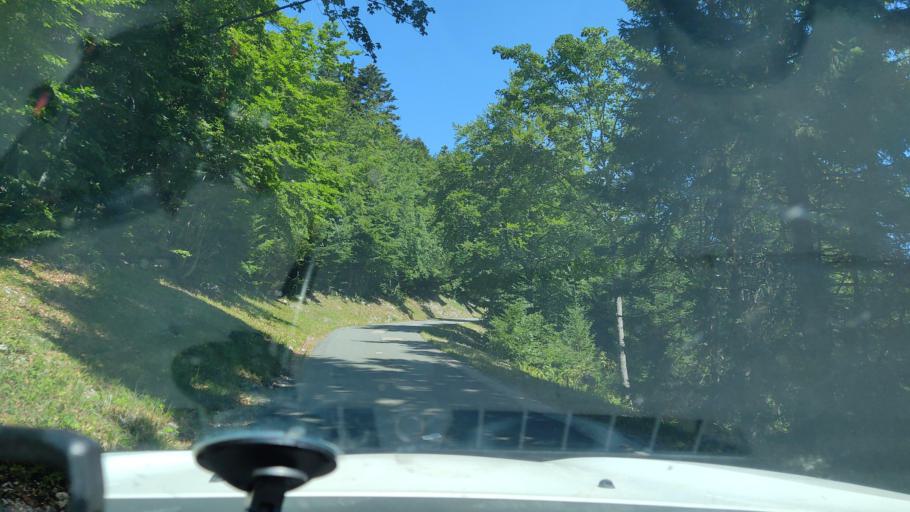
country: FR
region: Rhone-Alpes
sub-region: Departement de la Savoie
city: Le Bourget-du-Lac
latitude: 45.6616
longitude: 5.8242
